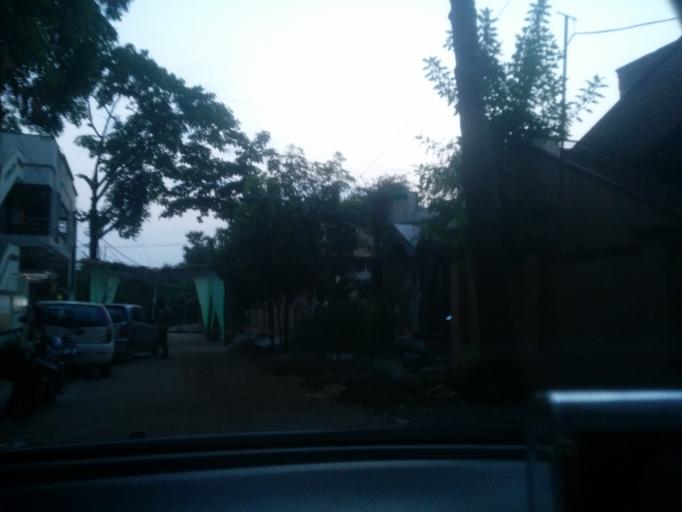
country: IN
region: Andhra Pradesh
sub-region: East Godavari
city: Rajahmundry
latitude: 17.0115
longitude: 81.8048
